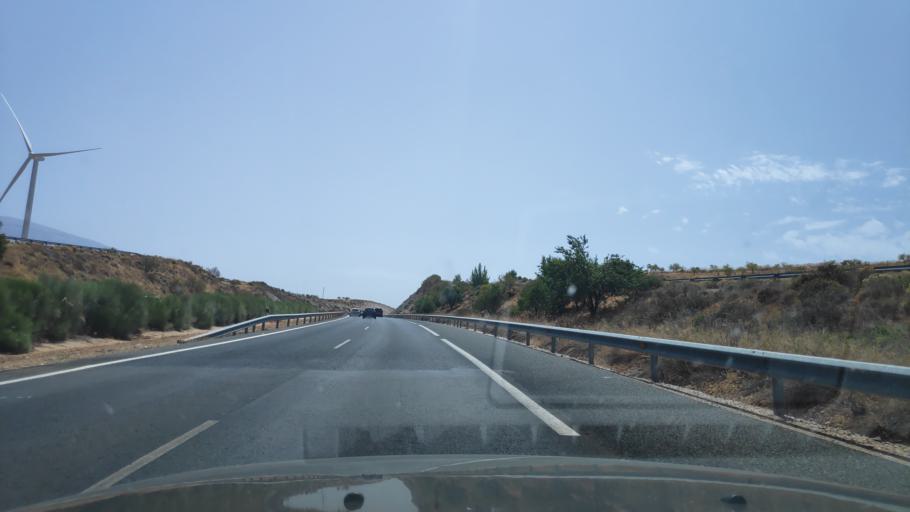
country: ES
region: Andalusia
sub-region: Provincia de Granada
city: Padul
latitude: 37.0047
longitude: -3.6367
